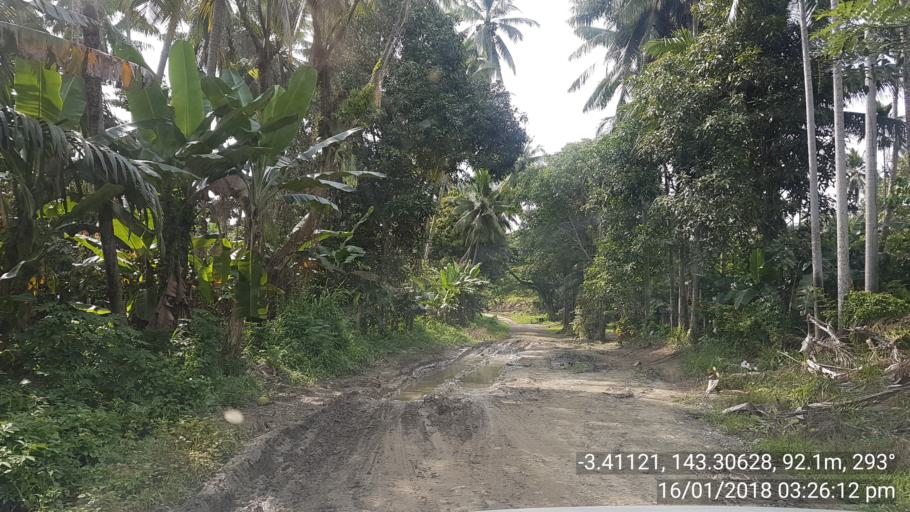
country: PG
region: East Sepik
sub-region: Wewak
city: Wewak
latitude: -3.4111
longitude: 143.3064
